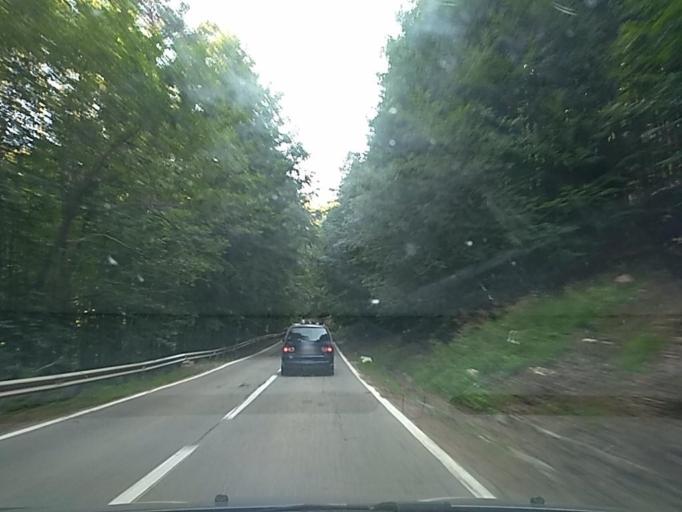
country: RO
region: Arges
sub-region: Comuna Arefu
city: Arefu
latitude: 45.3861
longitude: 24.6311
